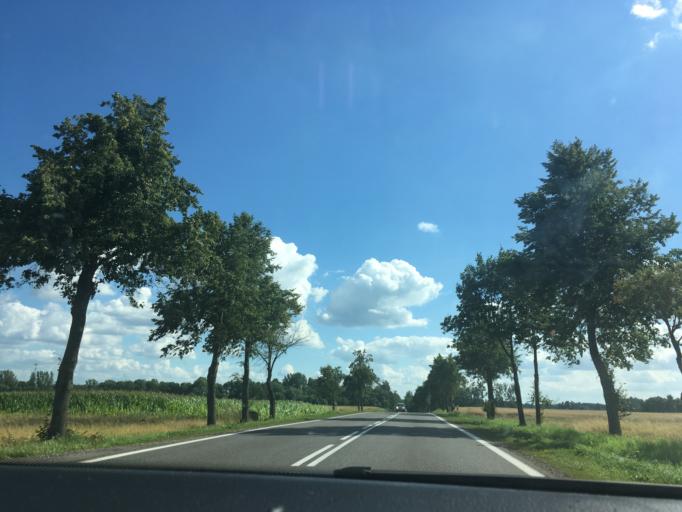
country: PL
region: Podlasie
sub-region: Powiat sokolski
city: Janow
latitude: 53.4001
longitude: 23.1156
